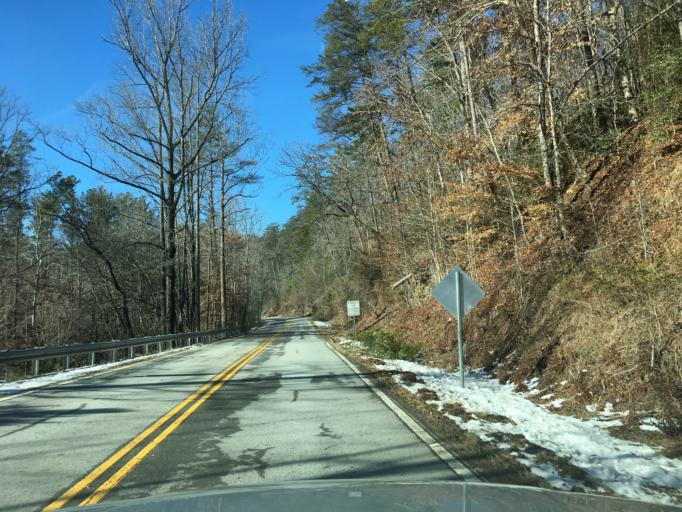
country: US
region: South Carolina
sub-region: Greenville County
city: Slater-Marietta
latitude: 35.0716
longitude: -82.6077
